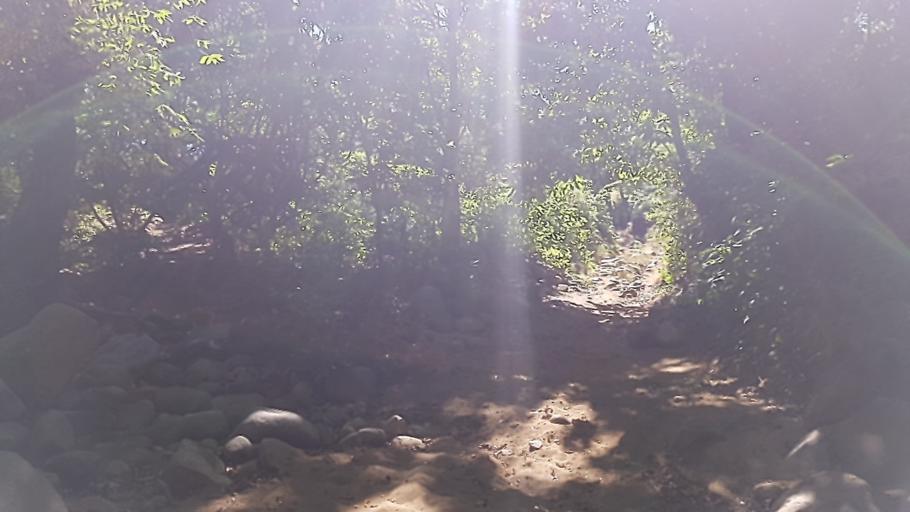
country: NI
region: Carazo
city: Santa Teresa
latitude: 11.6618
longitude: -86.1767
